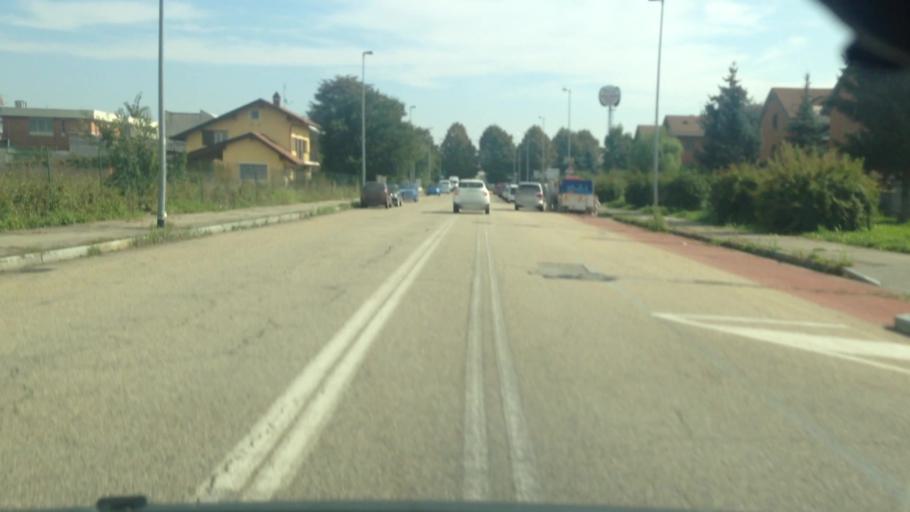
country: IT
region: Piedmont
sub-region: Provincia di Torino
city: Venaria Reale
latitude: 45.1171
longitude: 7.6406
